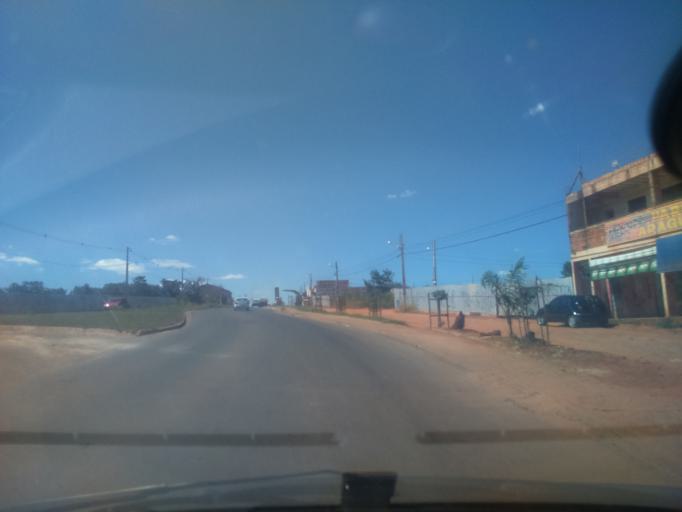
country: BR
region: Goias
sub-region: Luziania
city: Luziania
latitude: -16.1030
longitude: -47.9599
